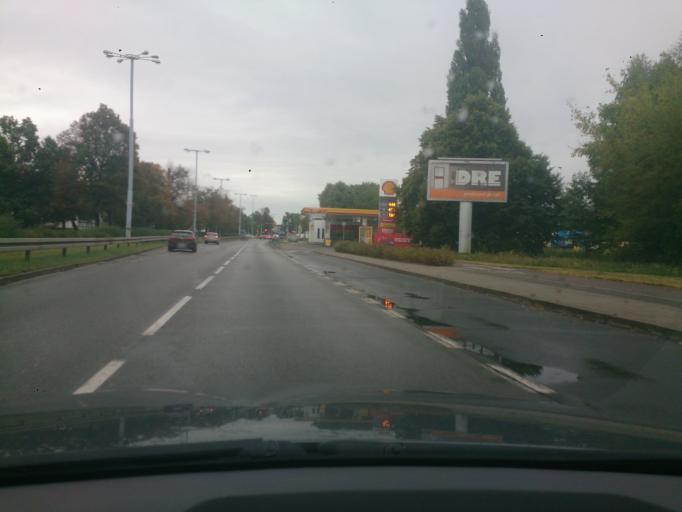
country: PL
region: Pomeranian Voivodeship
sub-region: Sopot
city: Sopot
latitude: 54.4166
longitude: 18.5657
